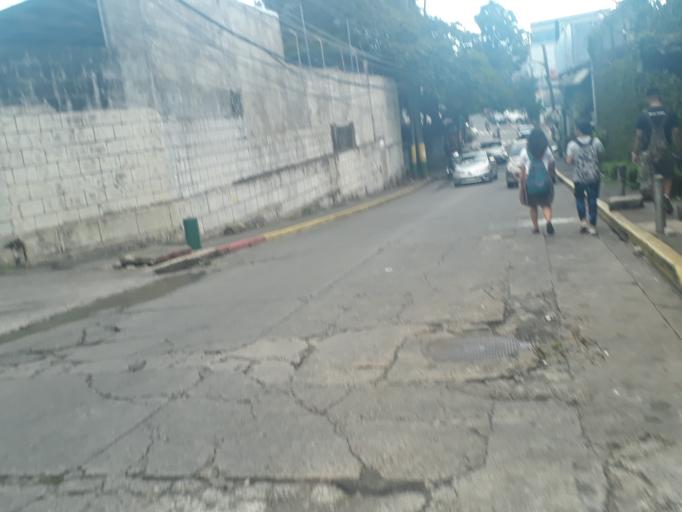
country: PH
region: Metro Manila
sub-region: Mandaluyong
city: Mandaluyong City
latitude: 14.5905
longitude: 121.0399
